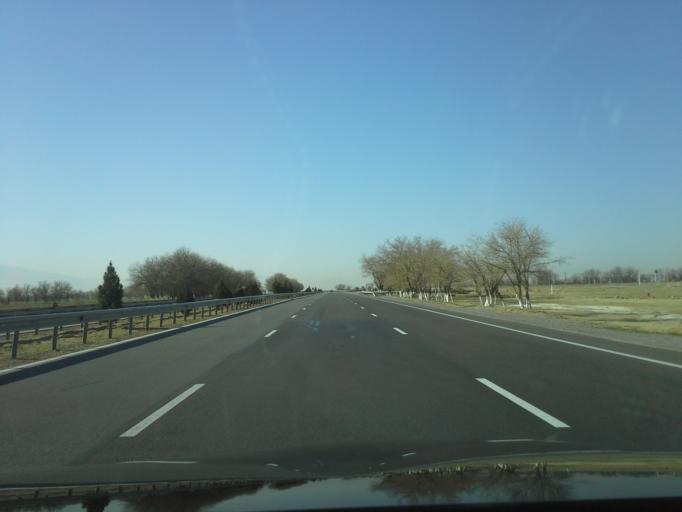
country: TM
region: Ahal
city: Annau
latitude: 37.8999
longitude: 58.5795
